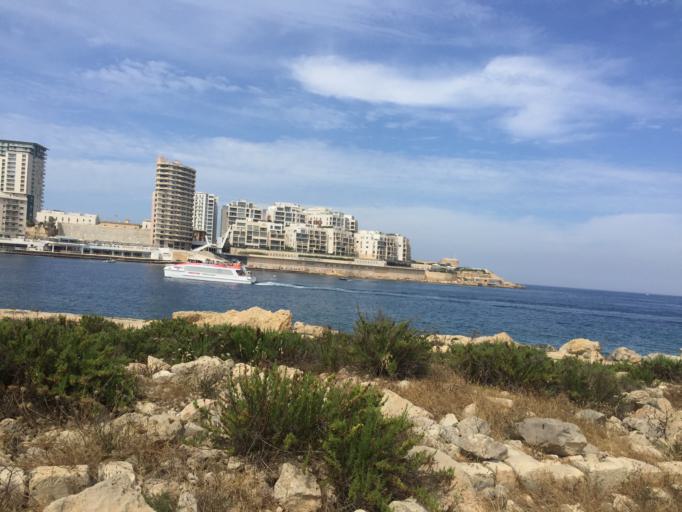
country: MT
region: Il-Furjana
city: Floriana
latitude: 35.9039
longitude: 14.5073
